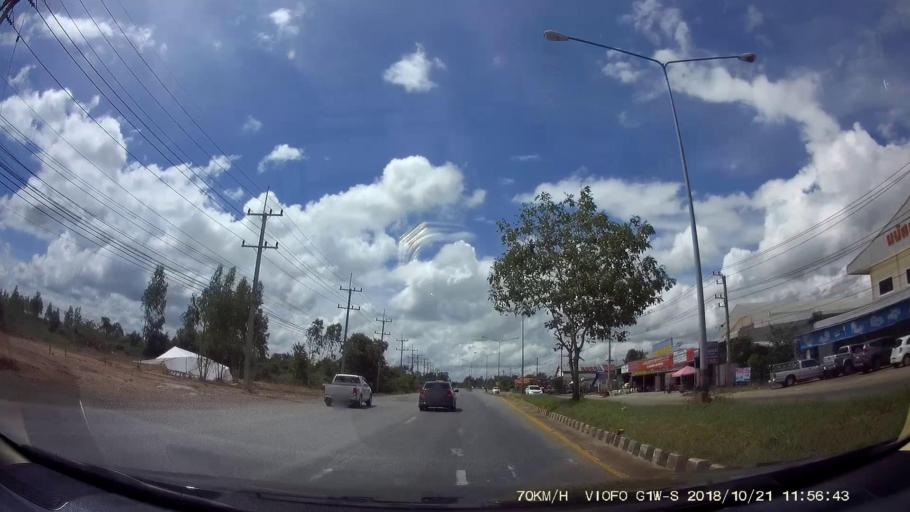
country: TH
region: Chaiyaphum
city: Chatturat
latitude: 15.5787
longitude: 101.8723
